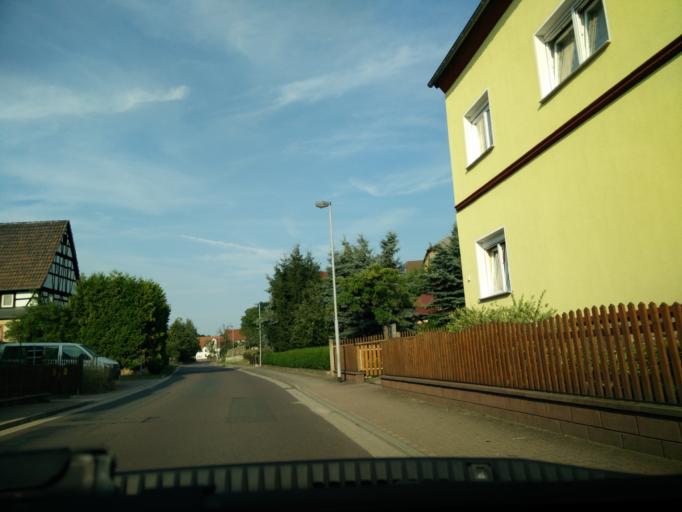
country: DE
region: Saxony
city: Frohburg
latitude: 51.0584
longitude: 12.5879
